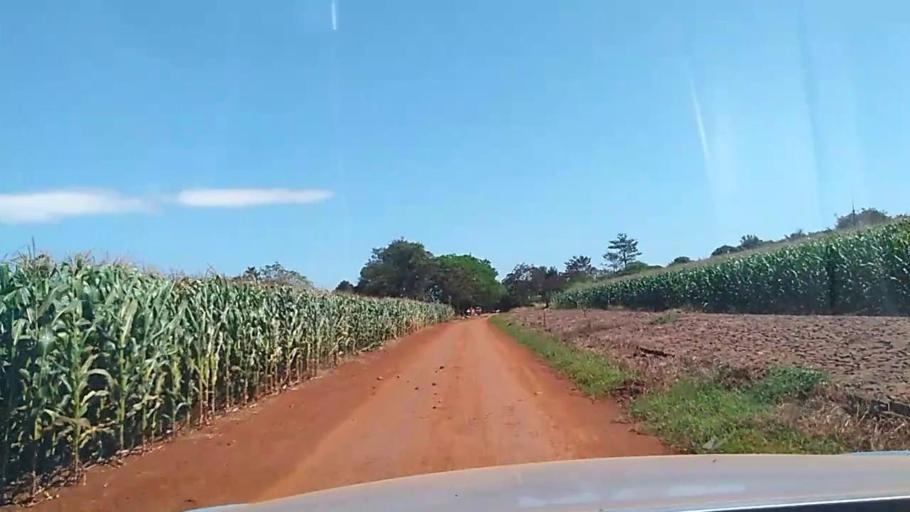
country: PY
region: Alto Parana
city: Naranjal
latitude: -25.9496
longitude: -55.1213
